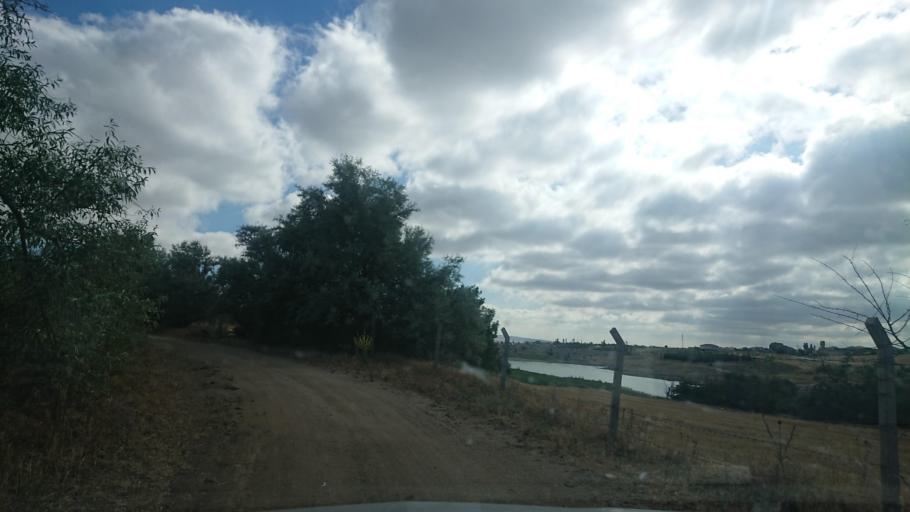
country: TR
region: Aksaray
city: Agacoren
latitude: 38.8629
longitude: 33.9439
